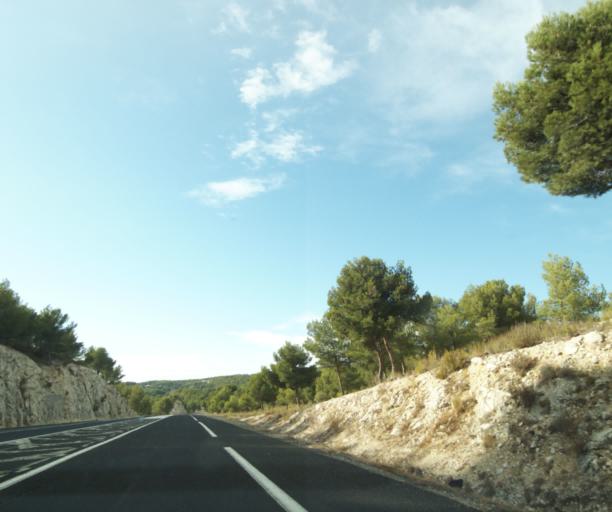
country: FR
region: Provence-Alpes-Cote d'Azur
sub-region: Departement des Bouches-du-Rhone
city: Sausset-les-Pins
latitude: 43.3418
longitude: 5.1019
